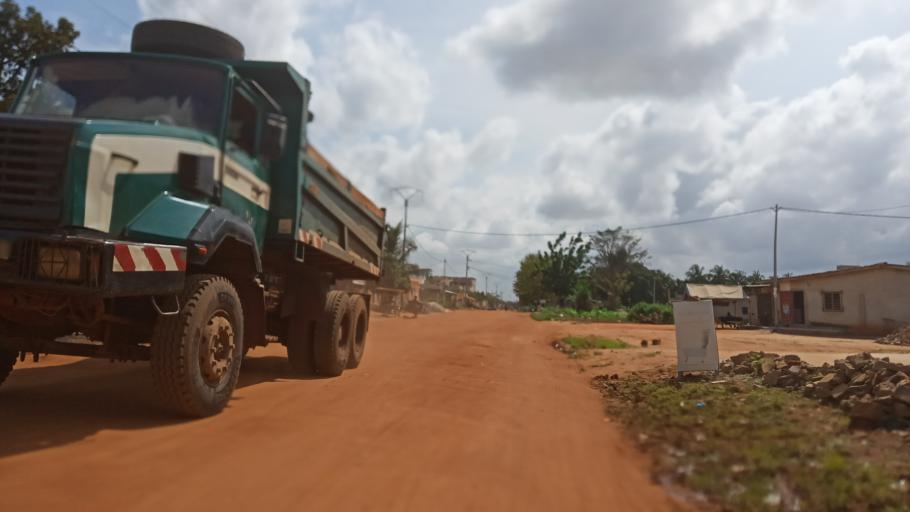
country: TG
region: Maritime
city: Lome
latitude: 6.2329
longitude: 1.1353
